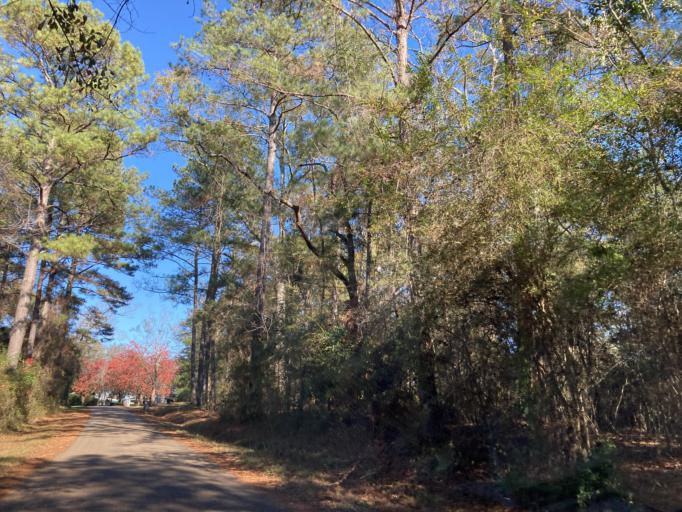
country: US
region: Mississippi
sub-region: Lamar County
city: Sumrall
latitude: 31.3340
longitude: -89.6124
